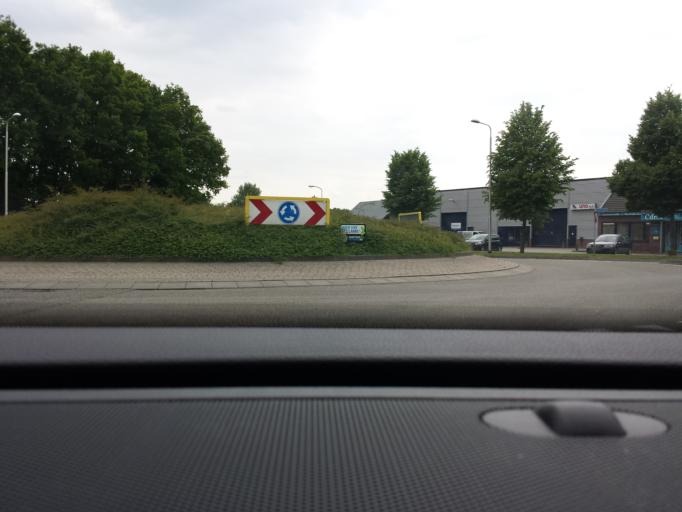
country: NL
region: Gelderland
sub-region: Gemeente Bronckhorst
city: Zelhem
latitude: 51.9988
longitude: 6.3539
